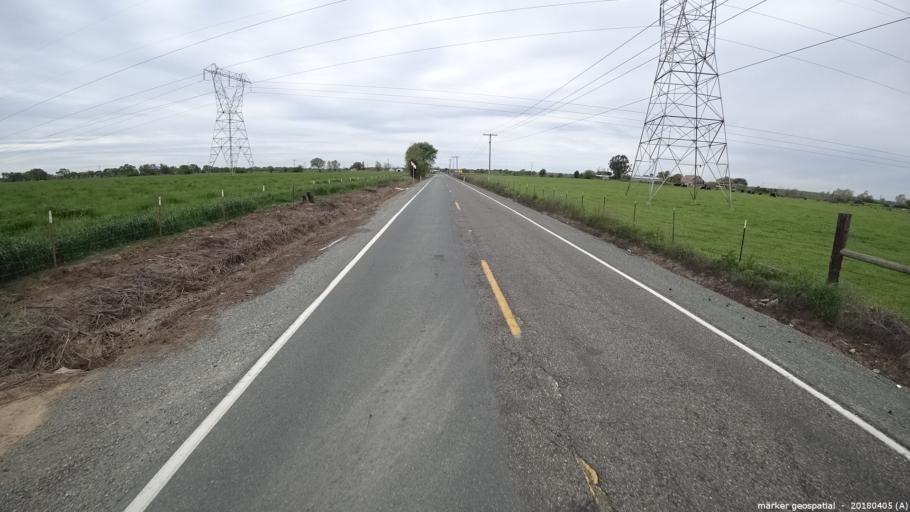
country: US
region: California
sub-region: San Joaquin County
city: Thornton
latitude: 38.2472
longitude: -121.3657
